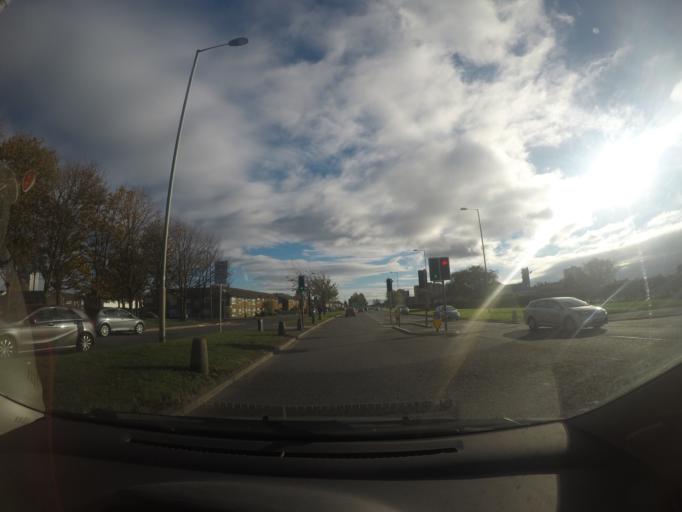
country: GB
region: England
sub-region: City and Borough of Leeds
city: Scholes
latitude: 53.8262
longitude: -1.4578
